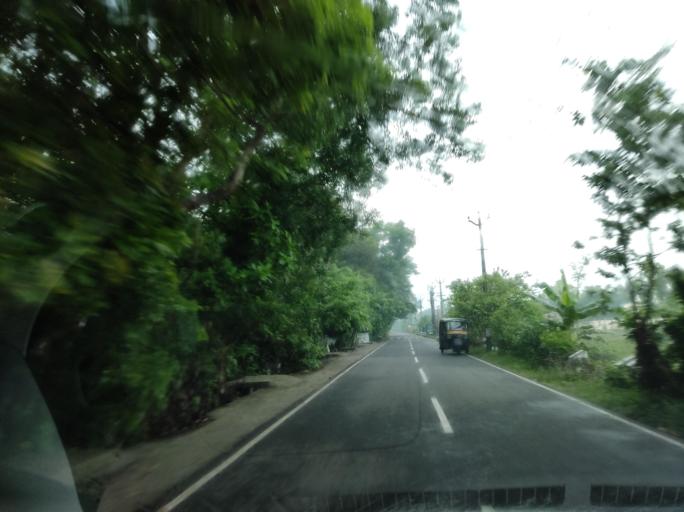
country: IN
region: Kerala
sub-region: Alappuzha
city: Alleppey
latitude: 9.5762
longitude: 76.3314
